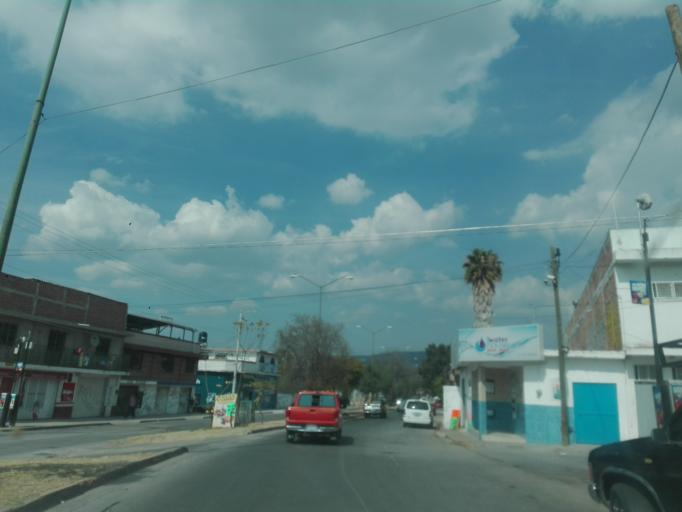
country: MX
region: Guanajuato
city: Leon
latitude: 21.1815
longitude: -101.6747
